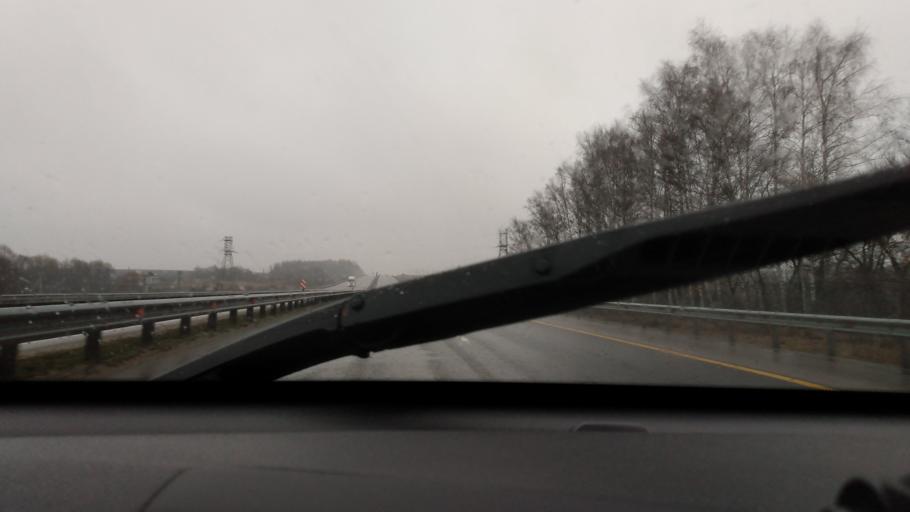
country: RU
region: Tula
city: Gritsovskiy
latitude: 54.2612
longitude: 38.1535
